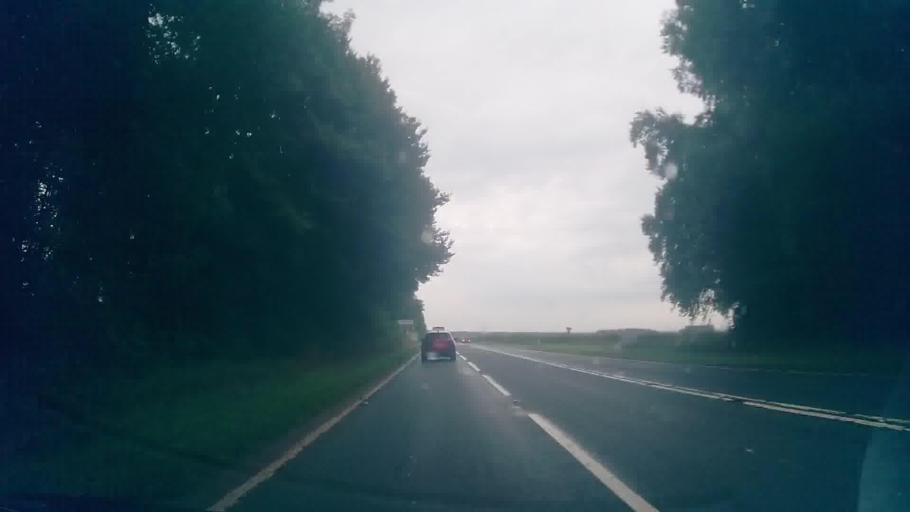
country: GB
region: Scotland
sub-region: Dumfries and Galloway
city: Annan
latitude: 55.0080
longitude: -3.3345
